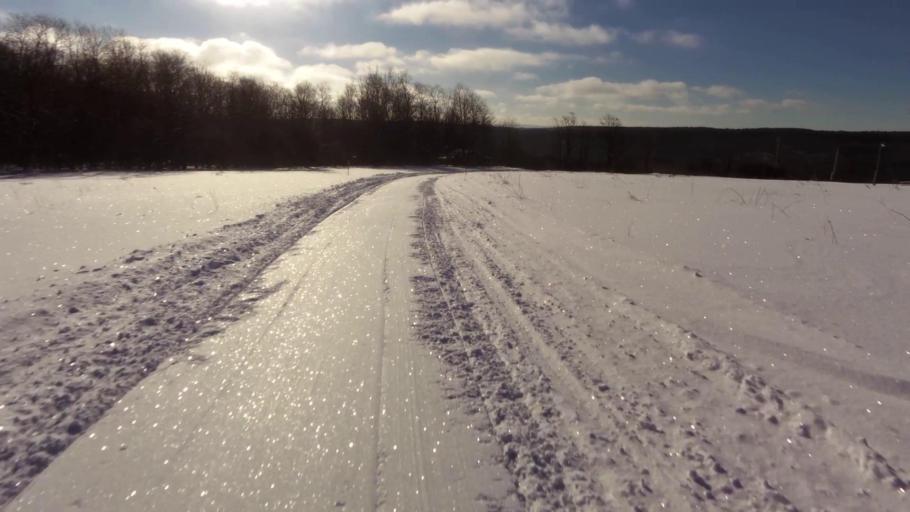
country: US
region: New York
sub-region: Chautauqua County
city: Falconer
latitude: 42.2620
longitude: -79.1816
